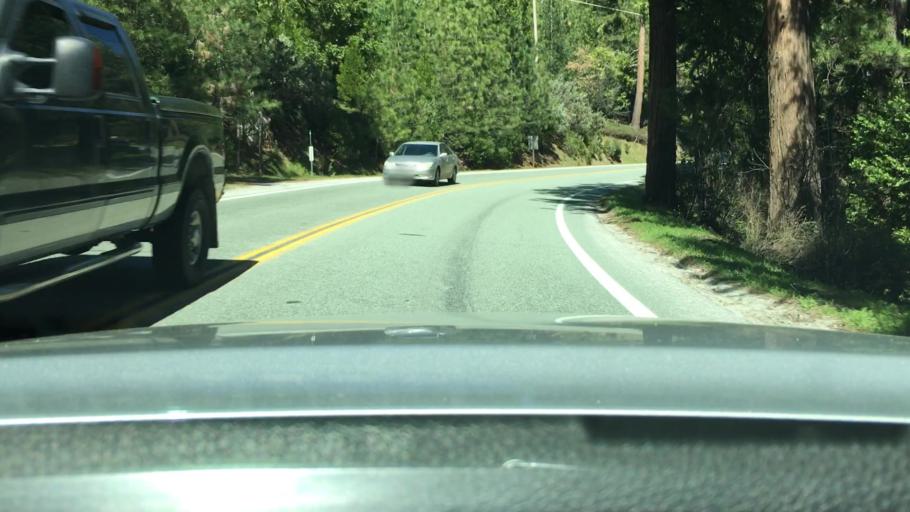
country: US
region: California
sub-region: Amador County
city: Pioneer
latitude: 38.4719
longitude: -120.5270
